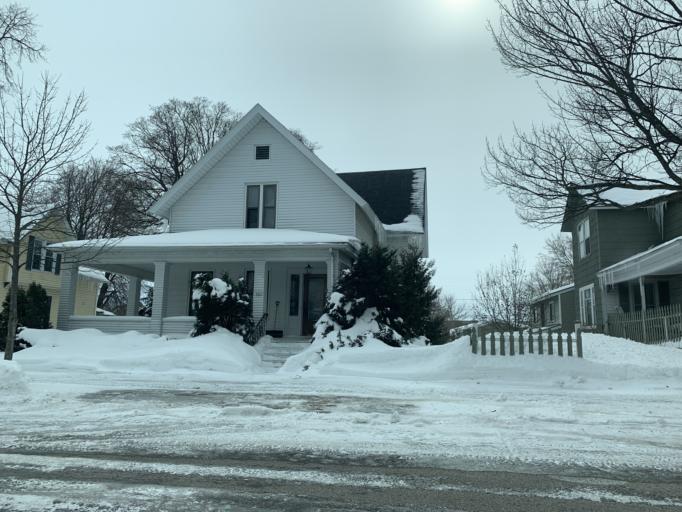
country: US
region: Michigan
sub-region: Menominee County
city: Menominee
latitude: 45.1029
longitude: -87.6098
